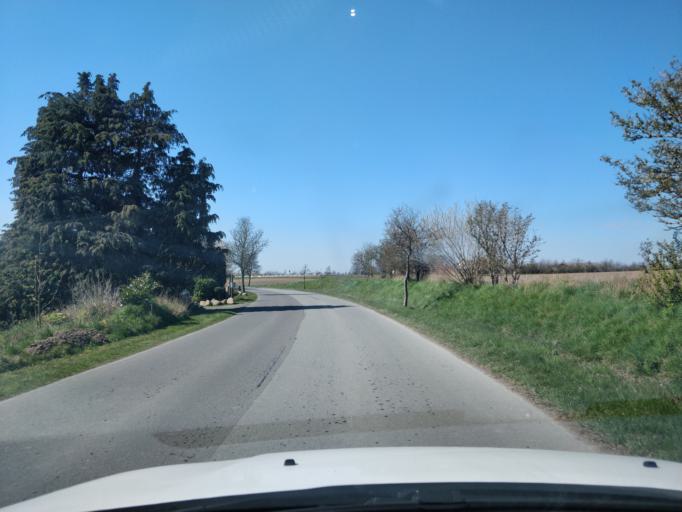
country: DK
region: Zealand
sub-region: Vordingborg Kommune
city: Stege
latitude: 54.9890
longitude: 12.3825
